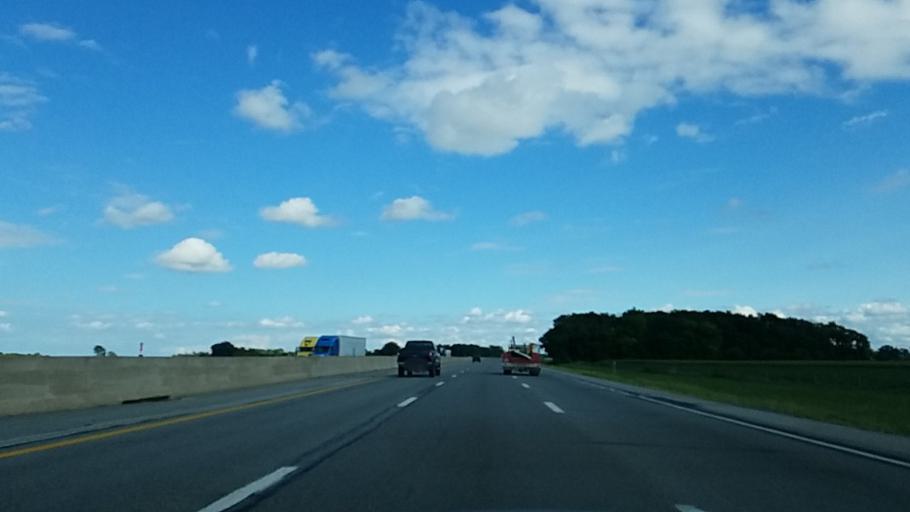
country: US
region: Ohio
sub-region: Sandusky County
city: Stony Prairie
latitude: 41.4216
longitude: -83.1701
